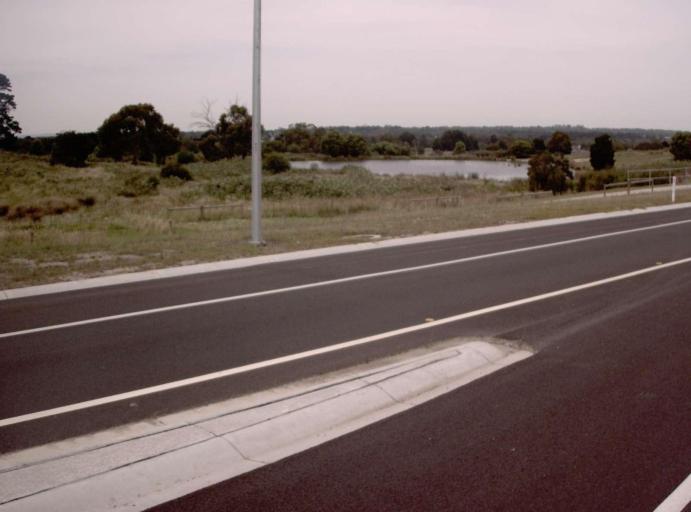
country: AU
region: Victoria
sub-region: Mornington Peninsula
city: Baxter
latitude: -38.1848
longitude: 145.1579
